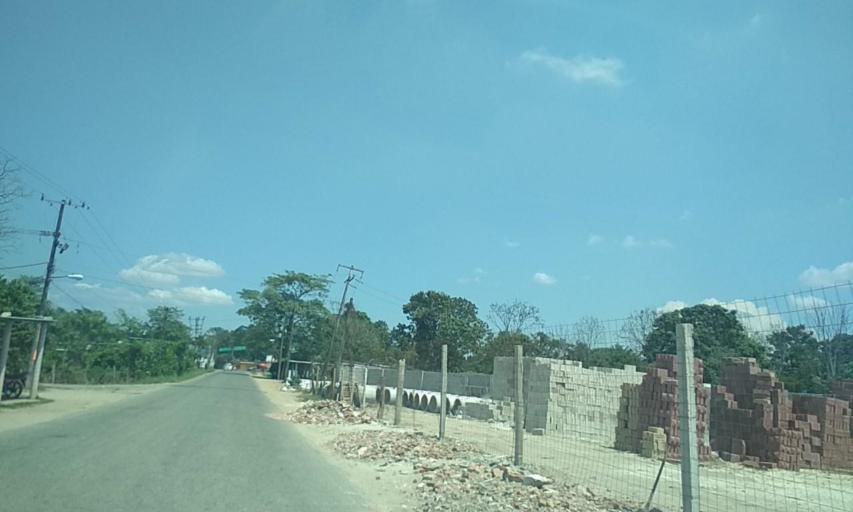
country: MX
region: Tabasco
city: Huimanguillo
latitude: 17.7917
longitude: -93.4395
